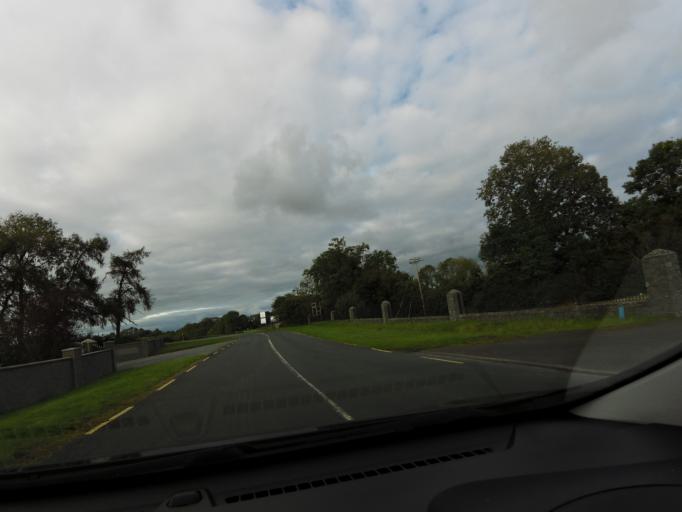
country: IE
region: Connaught
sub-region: County Galway
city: Ballinasloe
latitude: 53.3443
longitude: -8.0936
